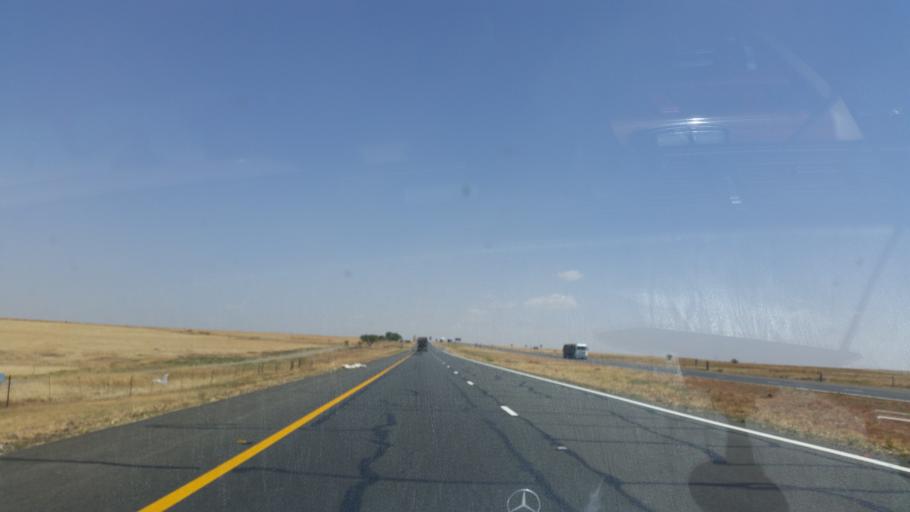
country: ZA
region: Orange Free State
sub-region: Lejweleputswa District Municipality
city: Brandfort
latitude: -28.8797
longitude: 26.5011
